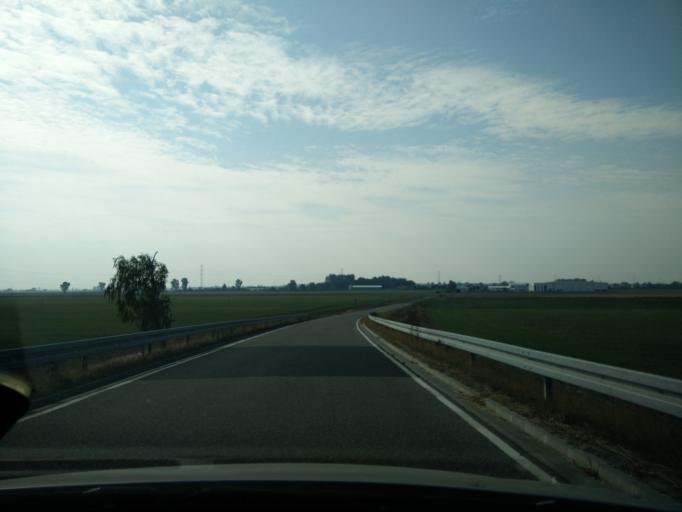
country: PL
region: Greater Poland Voivodeship
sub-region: Powiat sredzki
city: Dominowo
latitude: 52.3094
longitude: 17.3011
